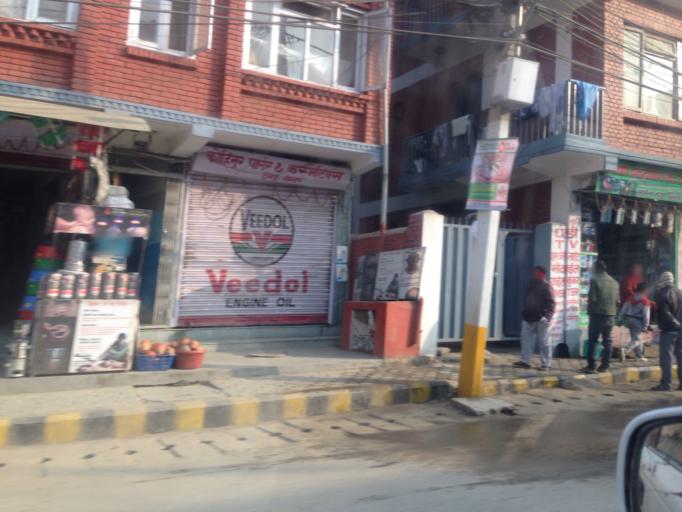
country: NP
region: Central Region
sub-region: Bagmati Zone
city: Kathmandu
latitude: 27.7082
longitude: 85.3346
